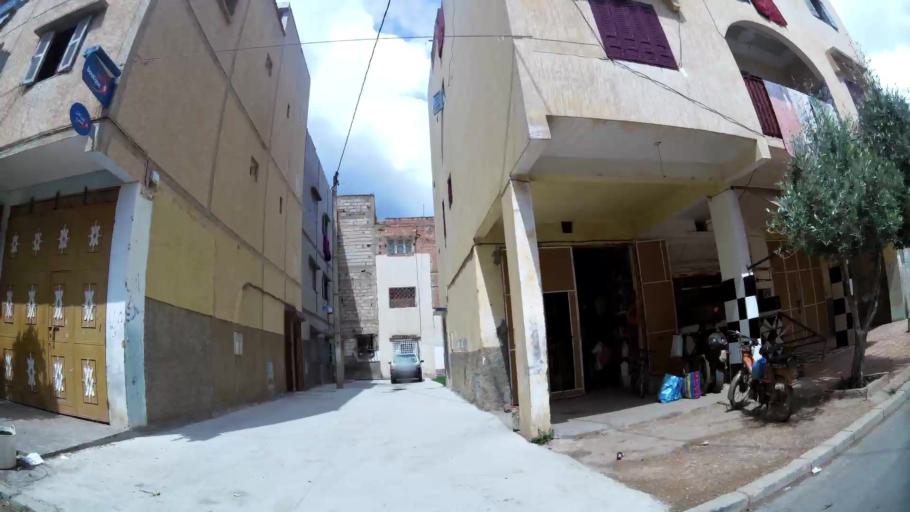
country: MA
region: Rabat-Sale-Zemmour-Zaer
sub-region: Khemisset
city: Tiflet
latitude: 33.8926
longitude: -6.3319
